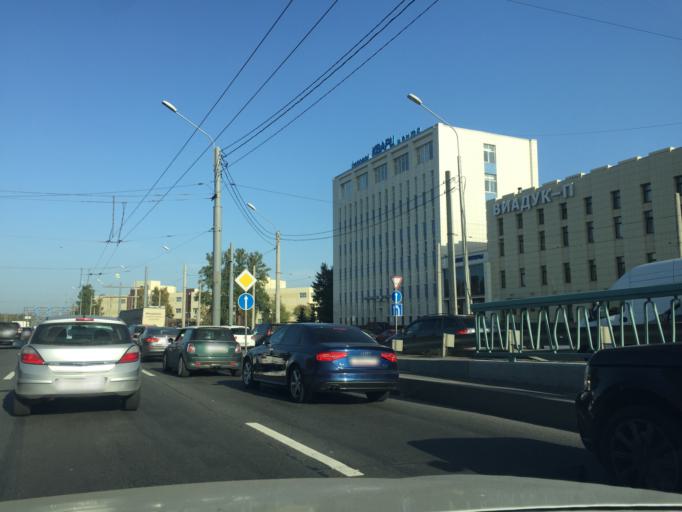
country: RU
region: St.-Petersburg
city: Krasnogvargeisky
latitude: 59.9938
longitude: 30.4358
